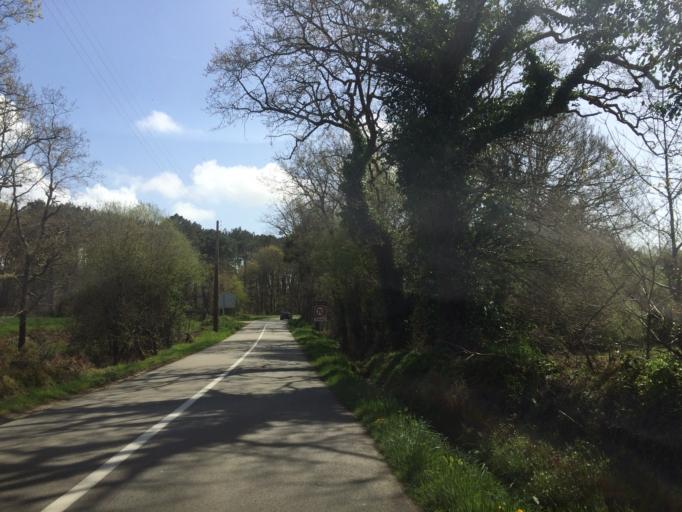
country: FR
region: Brittany
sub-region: Departement du Morbihan
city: Ploemel
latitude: 47.6380
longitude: -3.0478
